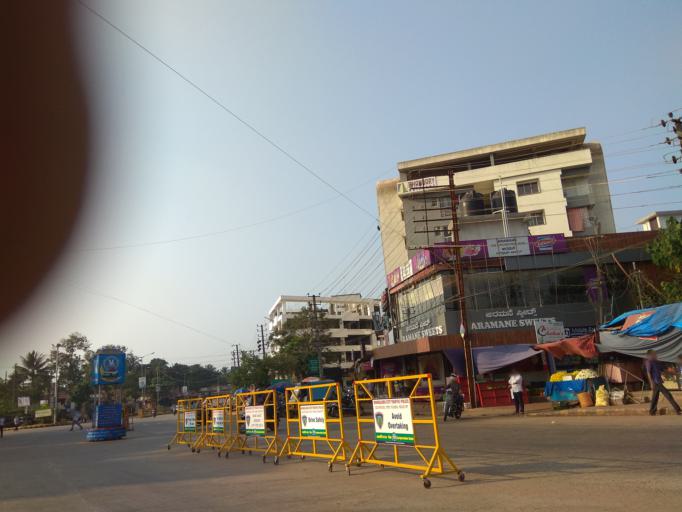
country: IN
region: Karnataka
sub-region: Dakshina Kannada
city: Mangalore
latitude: 12.9257
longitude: 74.8586
